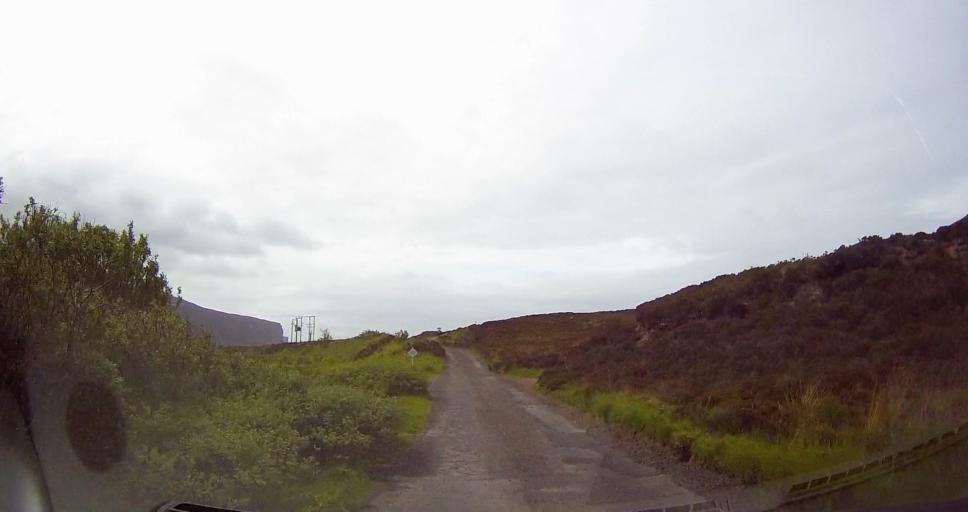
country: GB
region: Scotland
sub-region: Orkney Islands
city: Stromness
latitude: 58.8801
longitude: -3.3854
